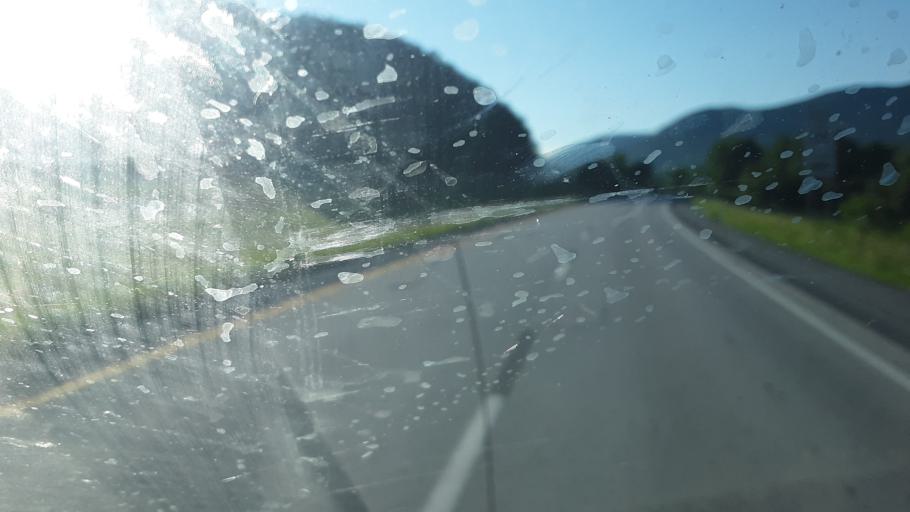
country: US
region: Vermont
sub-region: Rutland County
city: Castleton
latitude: 43.6167
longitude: -73.1583
